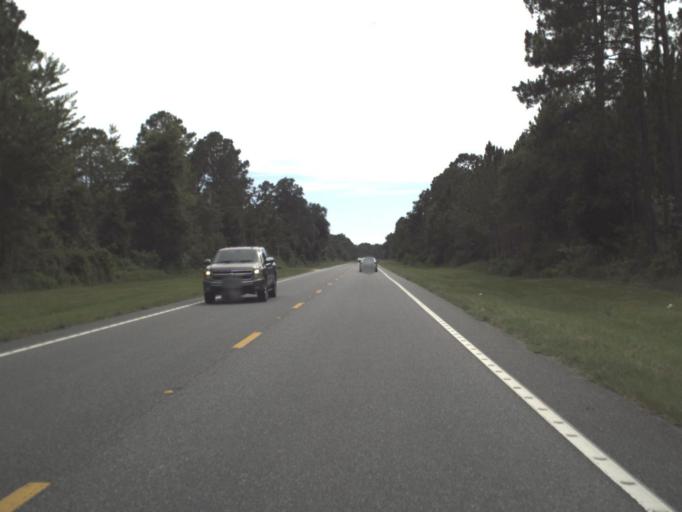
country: US
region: Florida
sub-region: Taylor County
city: Perry
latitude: 30.1152
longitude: -83.4131
